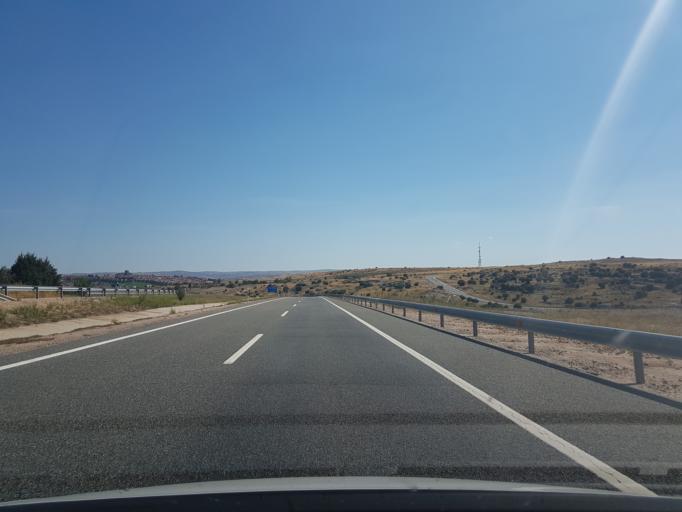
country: ES
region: Castille and Leon
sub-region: Provincia de Avila
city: Avila
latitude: 40.6738
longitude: -4.7270
